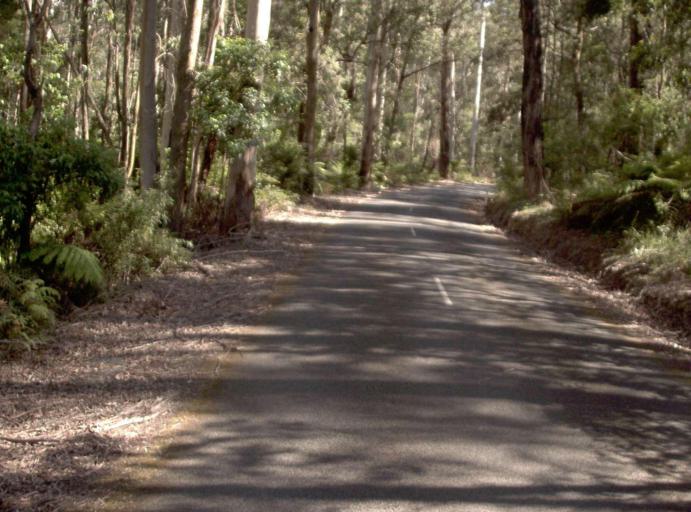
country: AU
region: Victoria
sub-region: East Gippsland
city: Lakes Entrance
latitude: -37.3910
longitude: 148.5971
